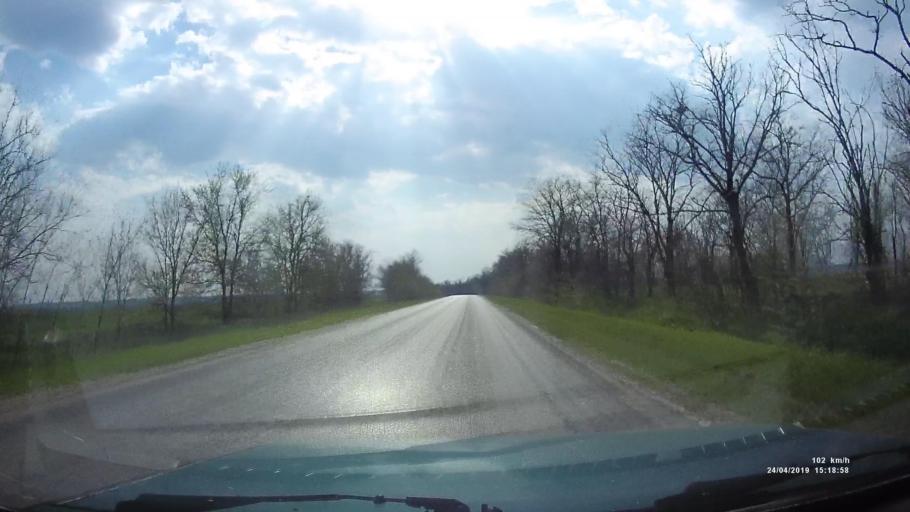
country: RU
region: Rostov
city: Remontnoye
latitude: 46.5430
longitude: 43.1558
